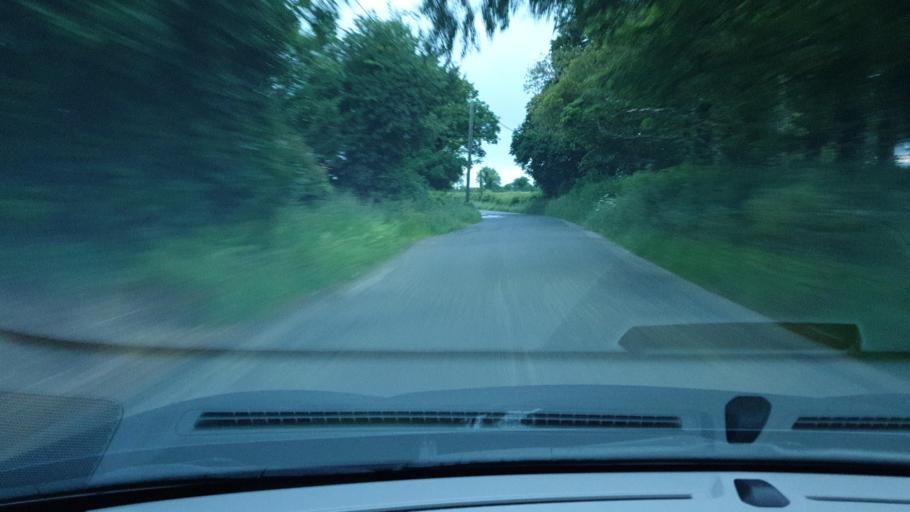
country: IE
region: Leinster
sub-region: An Mhi
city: Ashbourne
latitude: 53.5226
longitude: -6.3419
